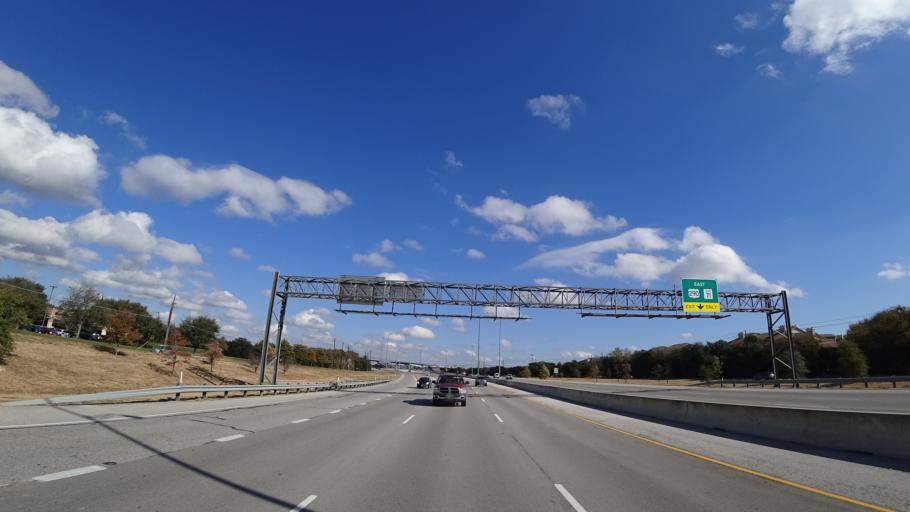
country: US
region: Texas
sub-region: Travis County
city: Rollingwood
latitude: 30.2285
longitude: -97.8293
